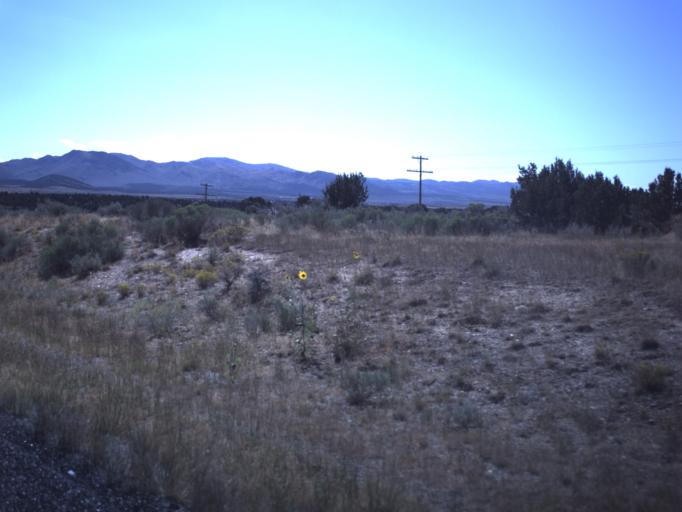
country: US
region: Utah
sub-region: Utah County
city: Genola
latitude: 39.9409
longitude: -112.1889
